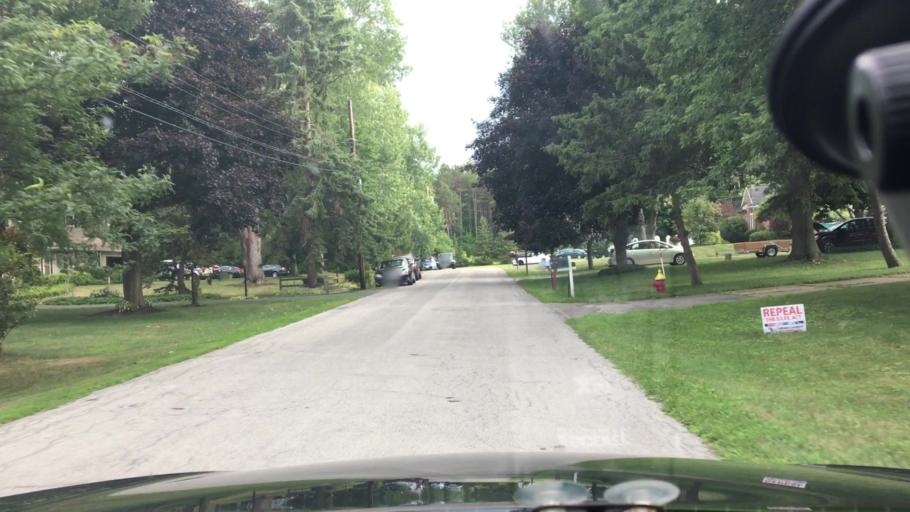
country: US
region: New York
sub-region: Erie County
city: Elma Center
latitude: 42.8194
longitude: -78.6587
